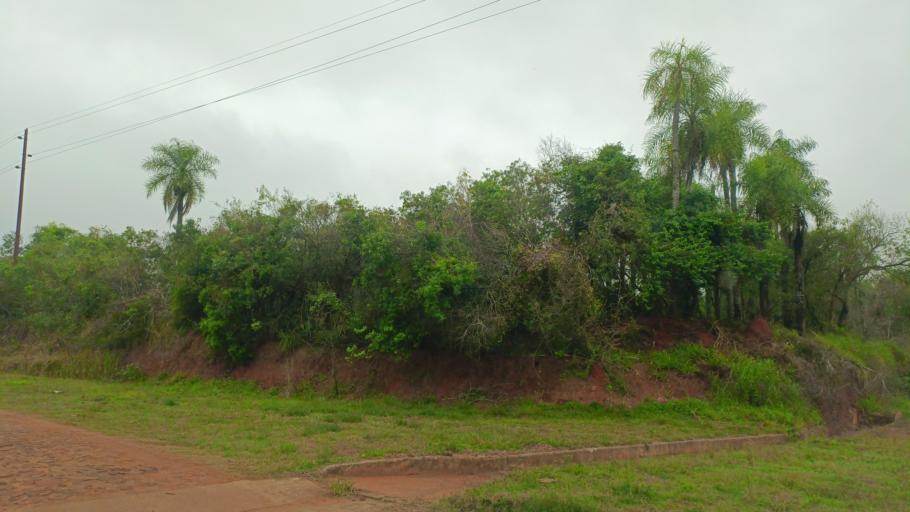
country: PY
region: Misiones
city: Santa Maria
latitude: -26.8723
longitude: -57.0119
